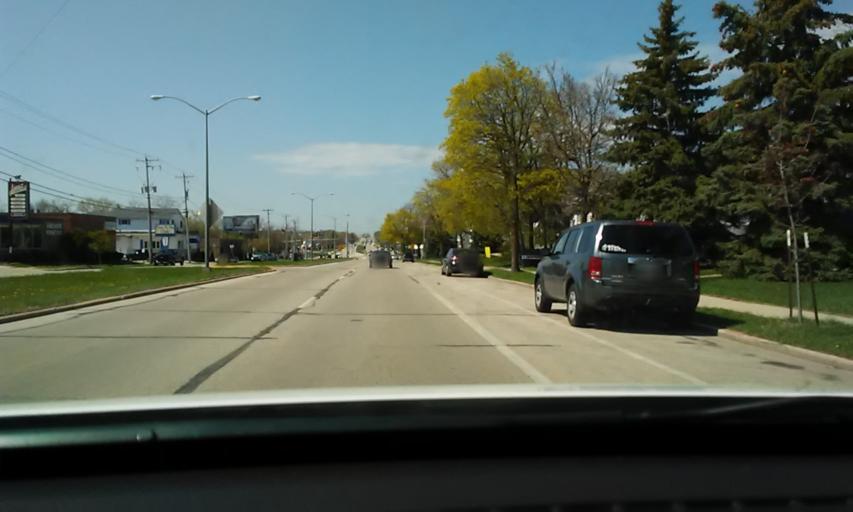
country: US
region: Wisconsin
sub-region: Milwaukee County
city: Greenfield
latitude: 42.9758
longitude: -87.9900
